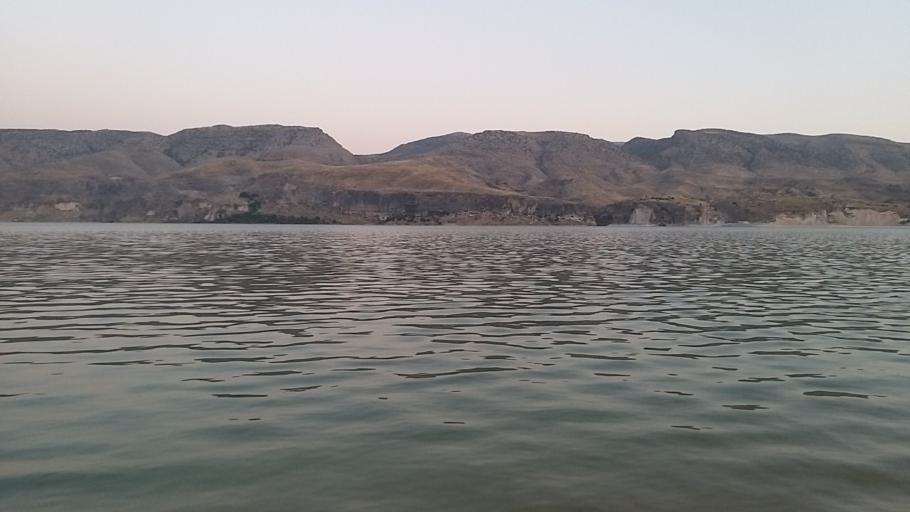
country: TR
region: Batman
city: Hasankeyf
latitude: 37.7232
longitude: 41.4150
